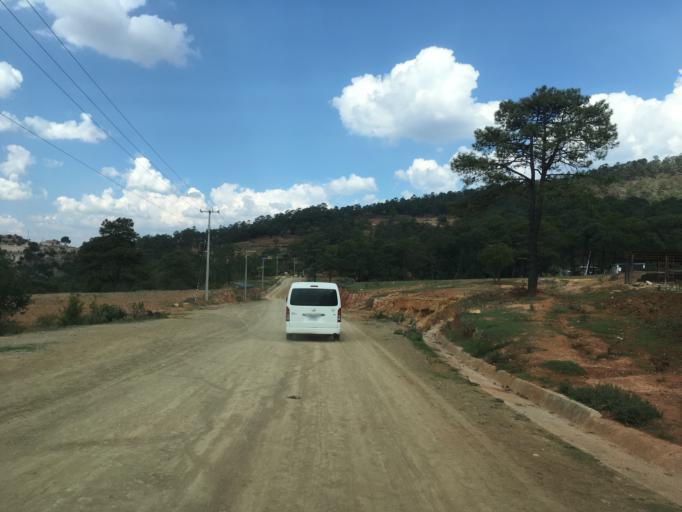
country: MX
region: Oaxaca
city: Santiago Tilantongo
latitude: 17.2178
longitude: -97.2759
